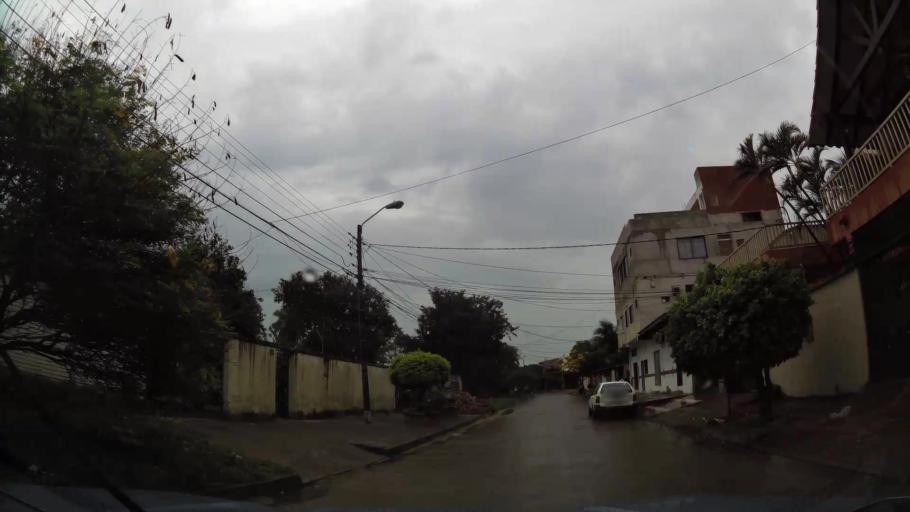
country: BO
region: Santa Cruz
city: Santa Cruz de la Sierra
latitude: -17.7827
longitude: -63.1582
